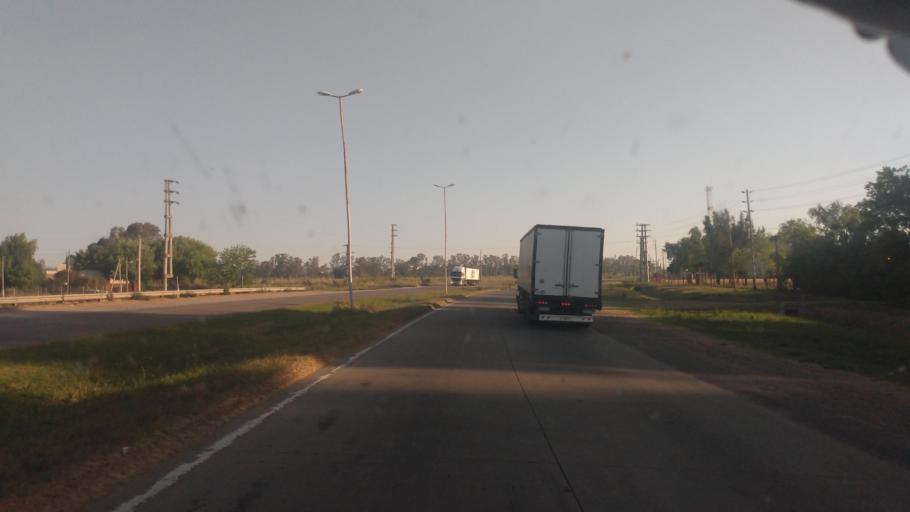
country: AR
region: Buenos Aires
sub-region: Partido de Campana
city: Campana
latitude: -34.2531
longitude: -58.9644
